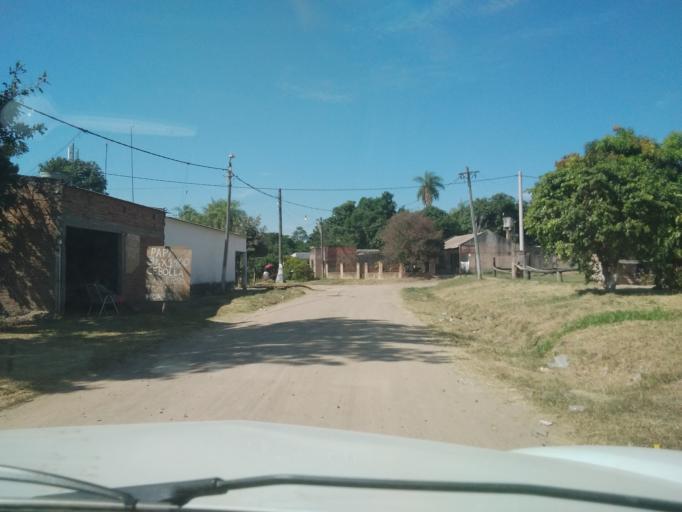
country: AR
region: Corrientes
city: Corrientes
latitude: -27.5102
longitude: -58.8051
